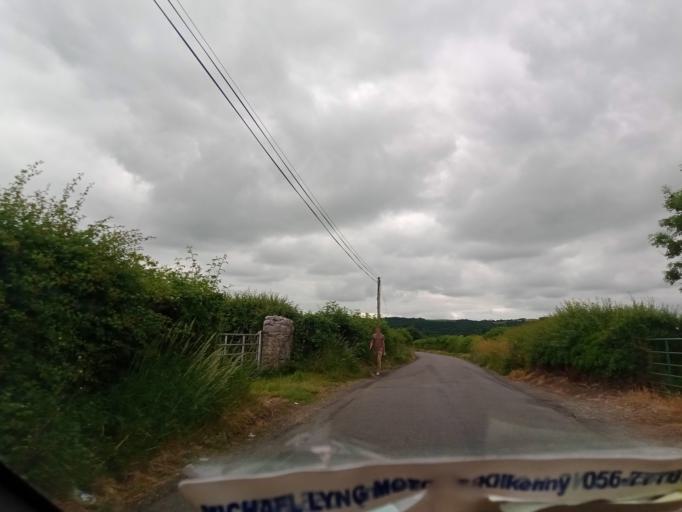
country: IE
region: Leinster
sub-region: Kilkenny
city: Ballyragget
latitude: 52.7379
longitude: -7.4159
